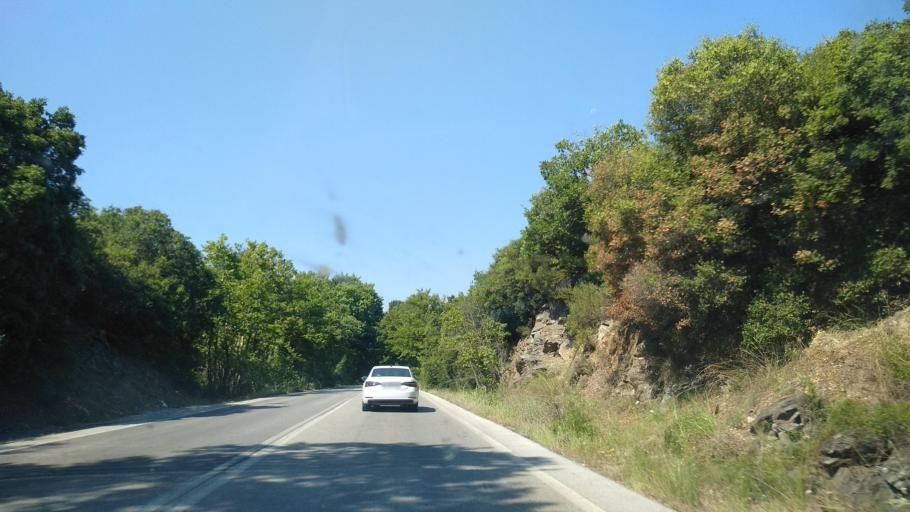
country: GR
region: Central Macedonia
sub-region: Nomos Thessalonikis
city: Stavros
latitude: 40.6631
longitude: 23.6392
